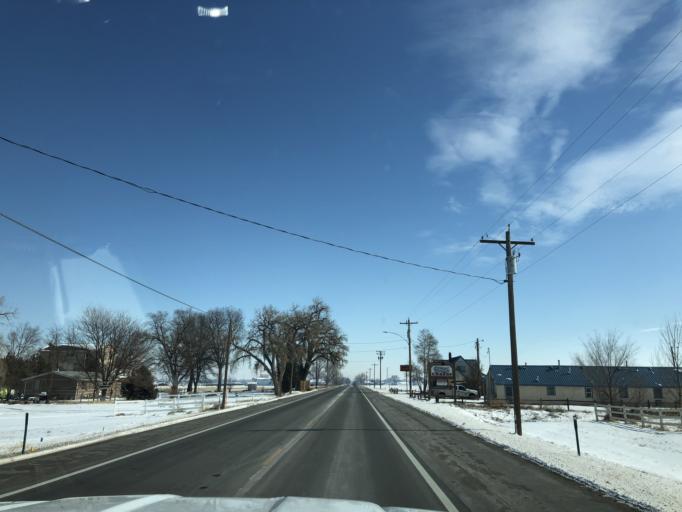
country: US
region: Colorado
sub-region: Morgan County
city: Fort Morgan
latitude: 40.2540
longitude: -103.8413
